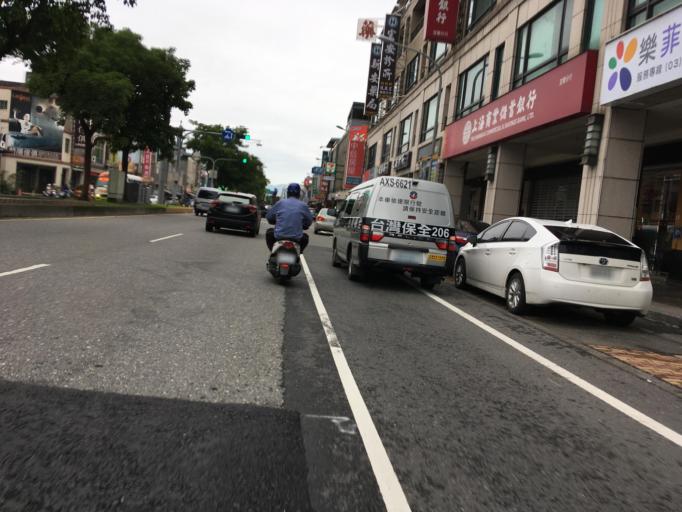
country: TW
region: Taiwan
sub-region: Yilan
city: Yilan
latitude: 24.6905
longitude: 121.7703
